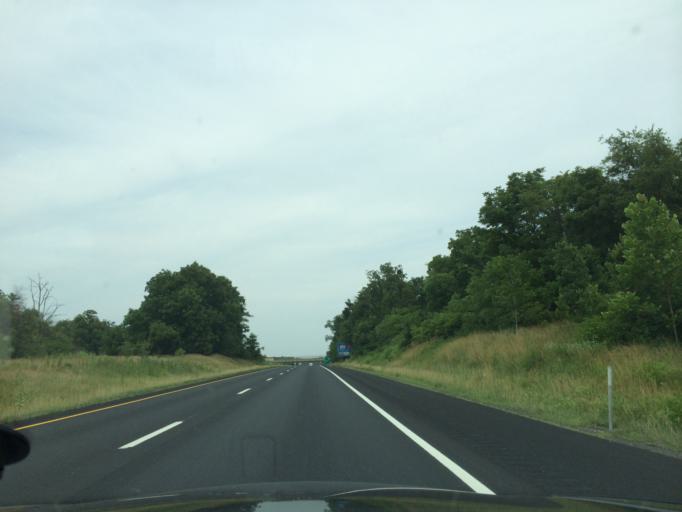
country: US
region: Maryland
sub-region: Washington County
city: Wilson-Conococheague
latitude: 39.6475
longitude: -77.9350
